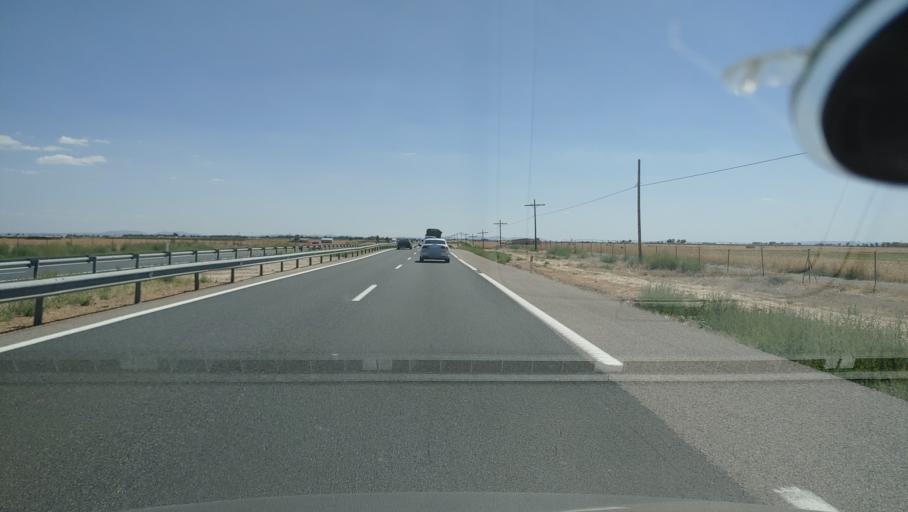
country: ES
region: Castille-La Mancha
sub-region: Provincia de Ciudad Real
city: Villarta de San Juan
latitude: 39.1534
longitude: -3.3881
